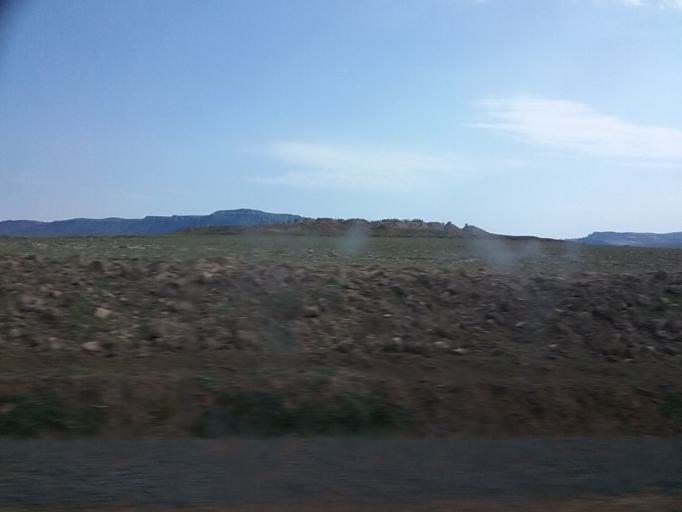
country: LS
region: Berea
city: Teyateyaneng
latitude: -29.0826
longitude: 27.9034
